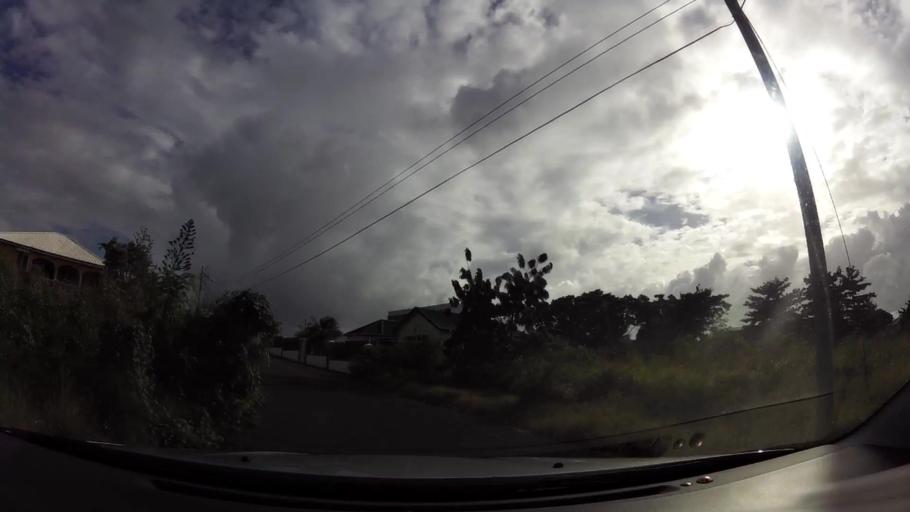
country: AG
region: Saint John
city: Saint John's
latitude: 17.1284
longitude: -61.8316
